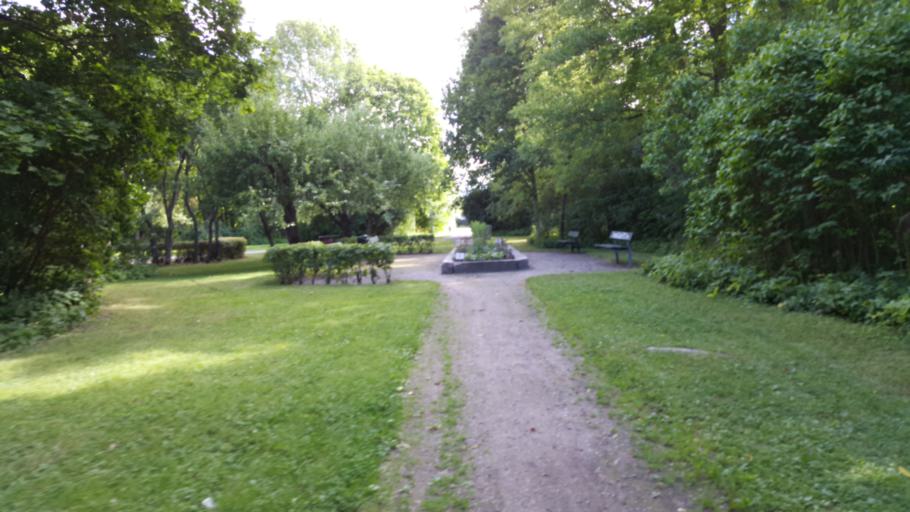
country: SE
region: Uppsala
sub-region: Uppsala Kommun
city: Gamla Uppsala
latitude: 59.8854
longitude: 17.6399
